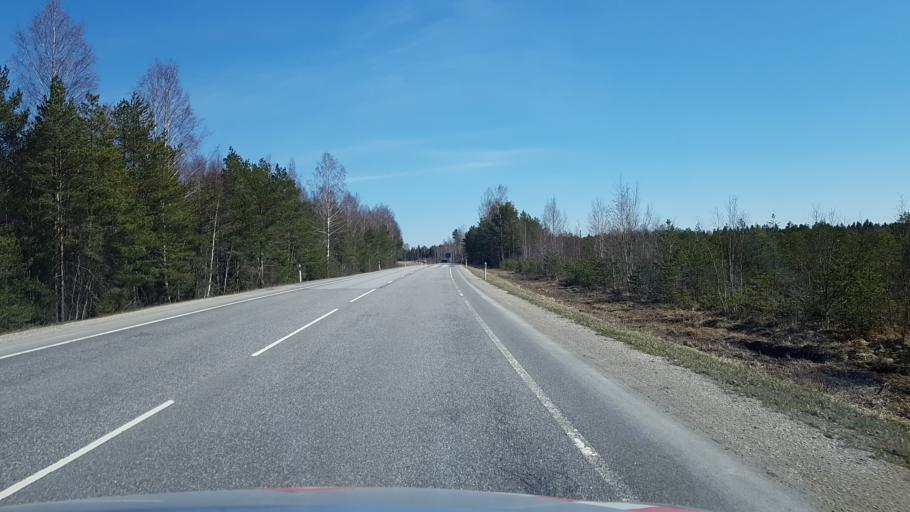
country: EE
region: Harju
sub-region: Nissi vald
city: Turba
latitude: 58.9941
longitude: 24.0460
